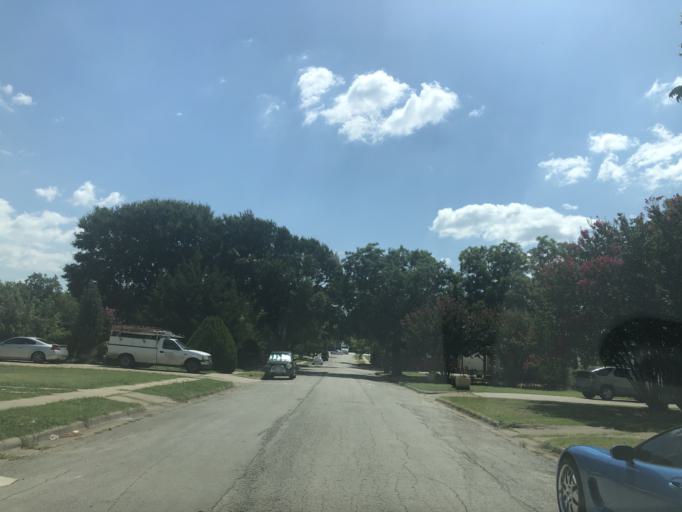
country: US
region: Texas
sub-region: Dallas County
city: Grand Prairie
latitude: 32.7421
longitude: -97.0283
